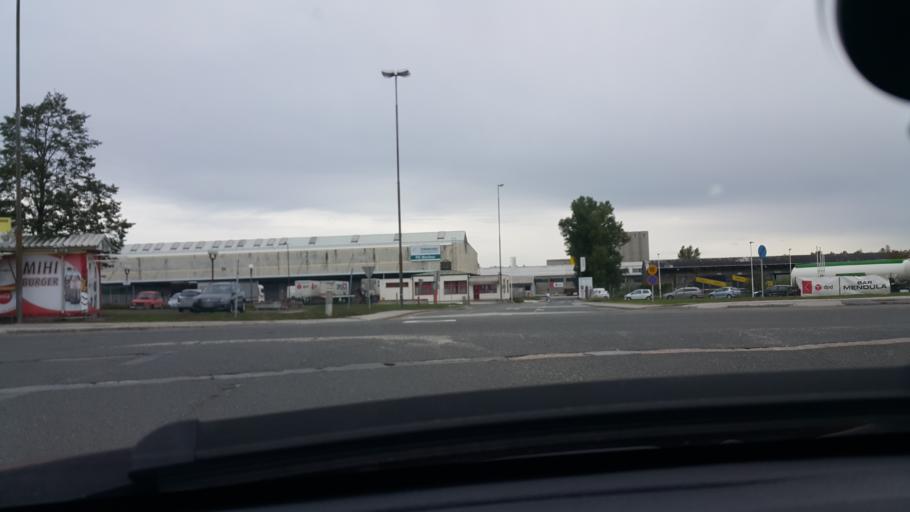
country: SI
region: Maribor
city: Razvanje
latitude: 46.5250
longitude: 15.6504
